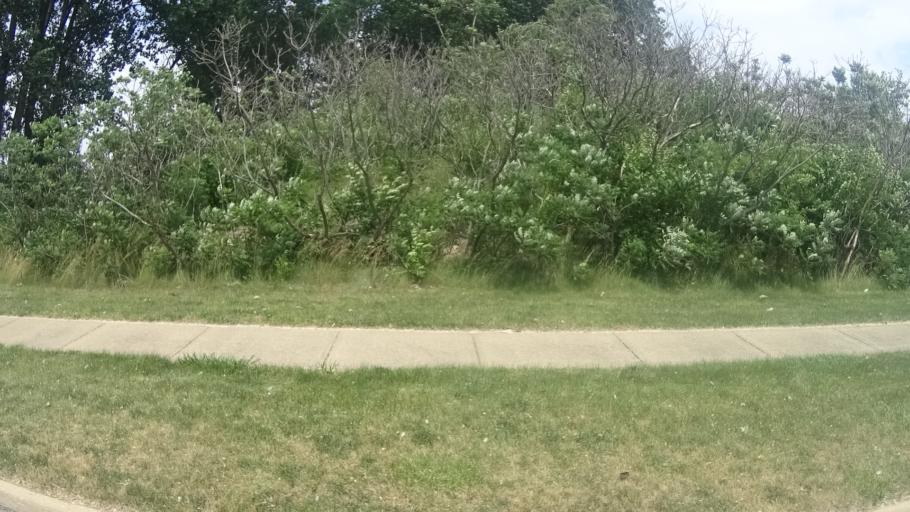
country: US
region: Ohio
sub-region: Erie County
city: Huron
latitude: 41.3868
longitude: -82.6398
